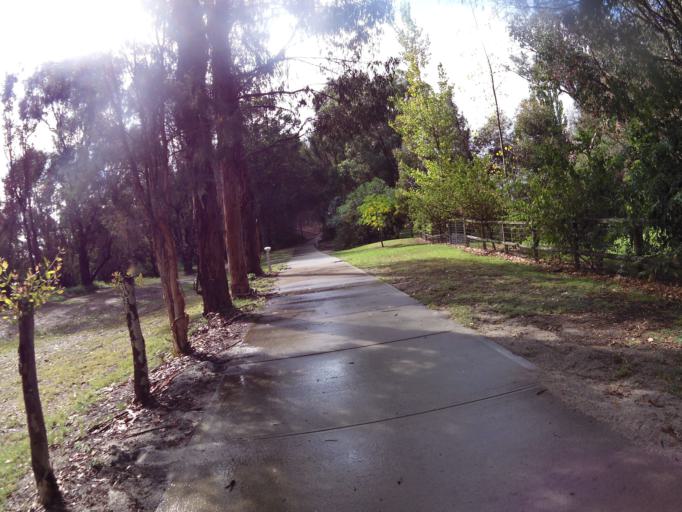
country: AU
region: Western Australia
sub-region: Donnybrook-Balingup
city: Donnybrook
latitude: -33.5723
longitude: 115.8259
